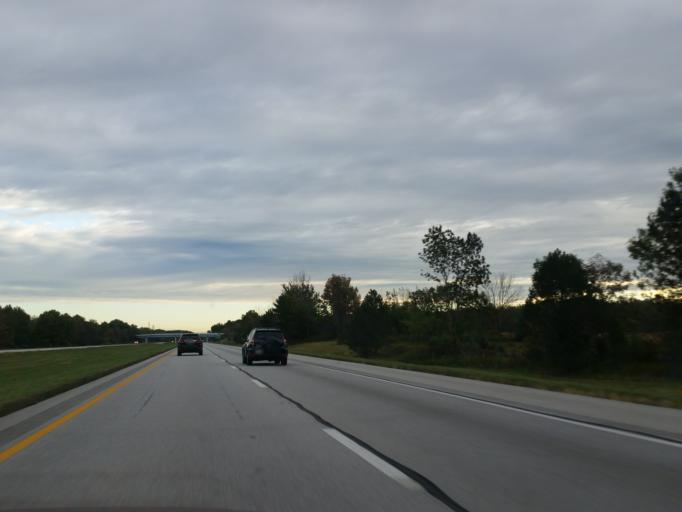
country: US
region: Ohio
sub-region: Ashtabula County
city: North Kingsville
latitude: 41.8649
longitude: -80.6851
